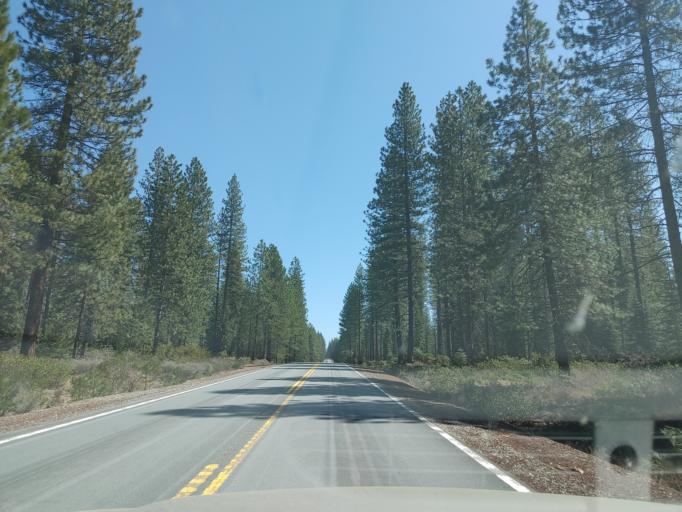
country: US
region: California
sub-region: Siskiyou County
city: McCloud
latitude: 41.2671
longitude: -121.8985
